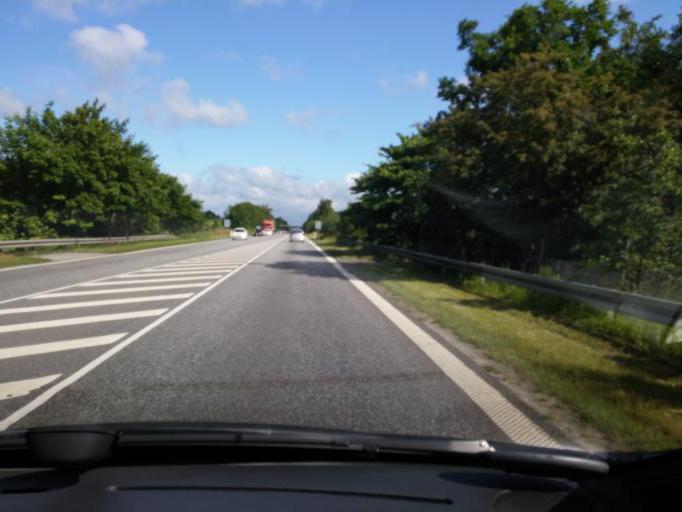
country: DK
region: Capital Region
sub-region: Hillerod Kommune
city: Hillerod
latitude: 55.9238
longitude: 12.2574
